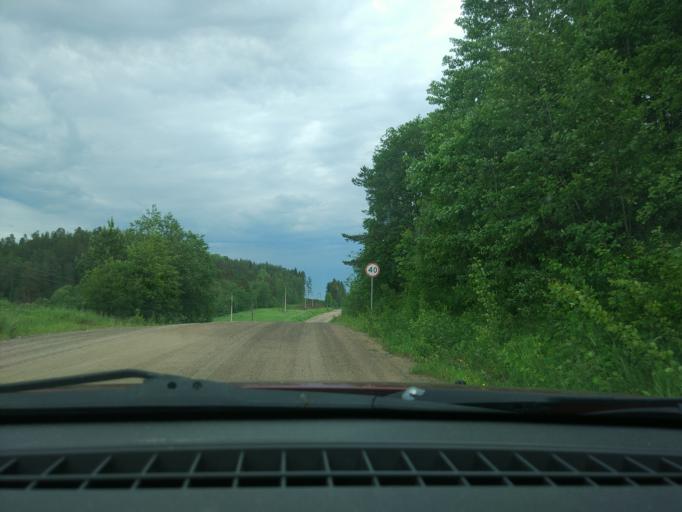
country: RU
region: Leningrad
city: Kuznechnoye
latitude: 61.2701
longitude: 29.8342
